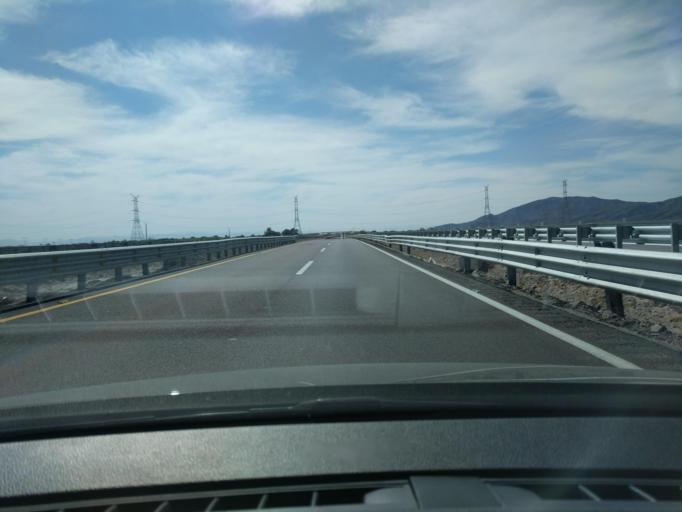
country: MX
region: Coahuila
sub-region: San Pedro
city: San Marcos
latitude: 25.5448
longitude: -103.0688
